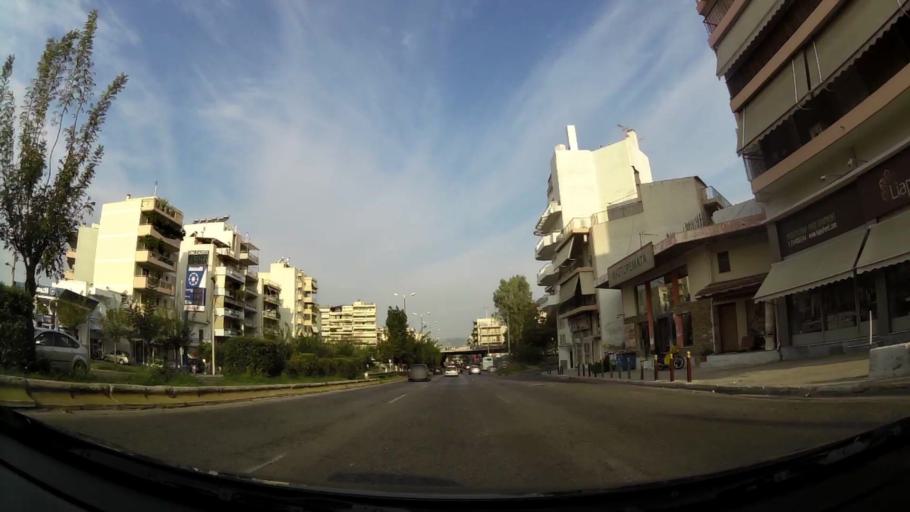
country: GR
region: Attica
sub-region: Nomarchia Athinas
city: Kallithea
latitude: 37.9638
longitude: 23.7077
